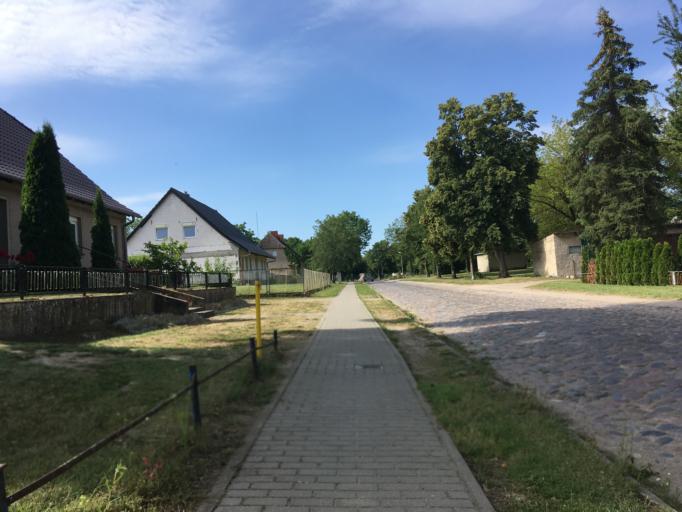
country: DE
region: Brandenburg
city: Gramzow
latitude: 53.2410
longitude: 14.0436
